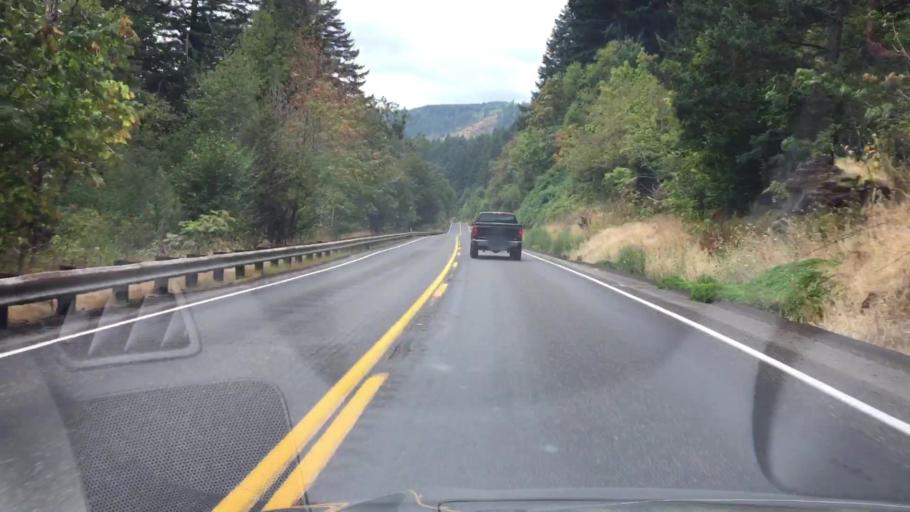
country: US
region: Washington
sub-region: Skamania County
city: Carson
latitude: 45.7168
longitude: -121.8076
